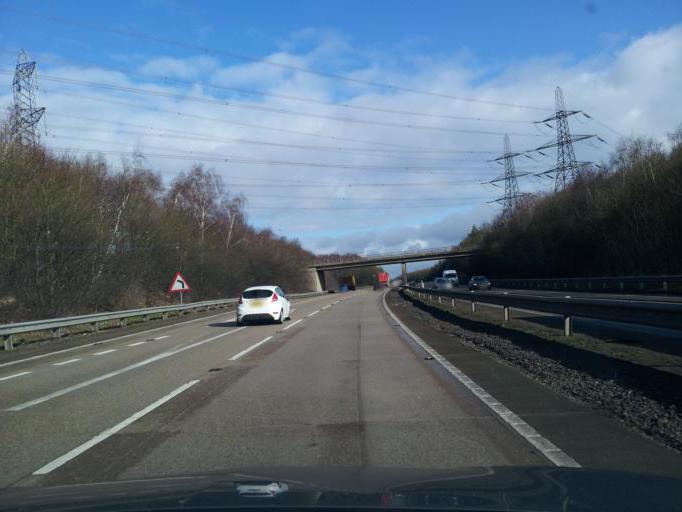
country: GB
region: England
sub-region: Suffolk
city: Bramford
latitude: 52.0856
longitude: 1.1118
